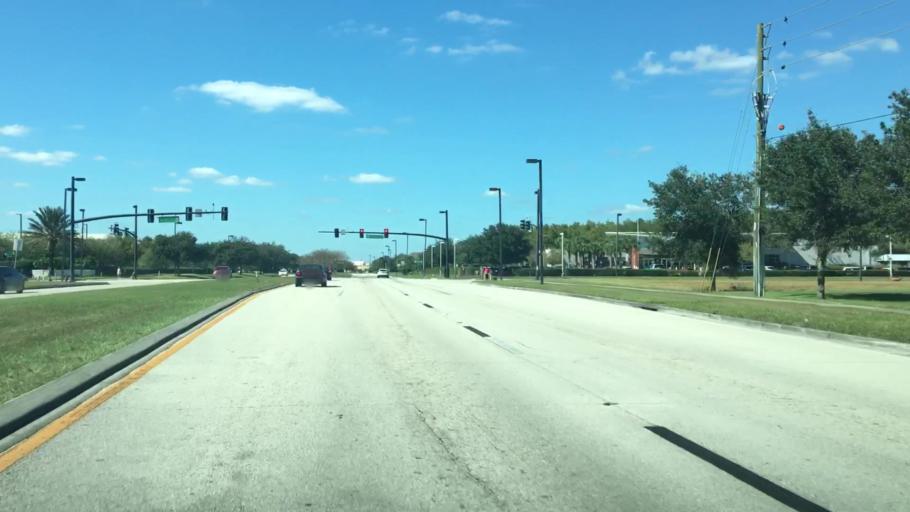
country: US
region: Florida
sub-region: Orange County
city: Conway
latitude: 28.4661
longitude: -81.2960
